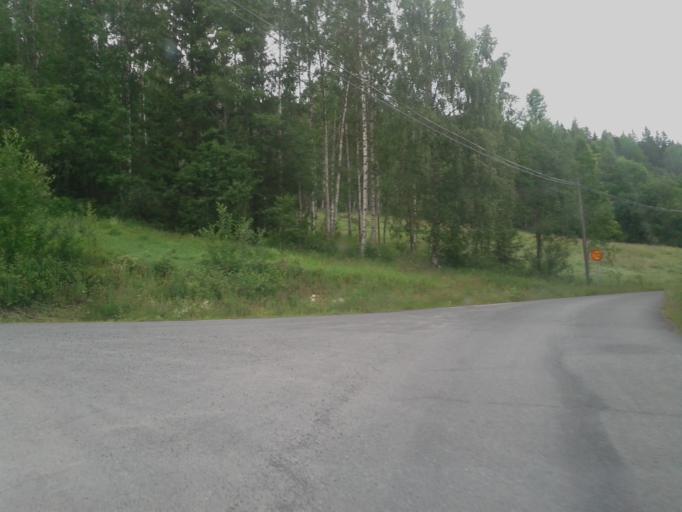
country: SE
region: Vaesternorrland
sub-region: OErnskoeldsviks Kommun
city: Bjasta
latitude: 63.0664
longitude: 18.4271
